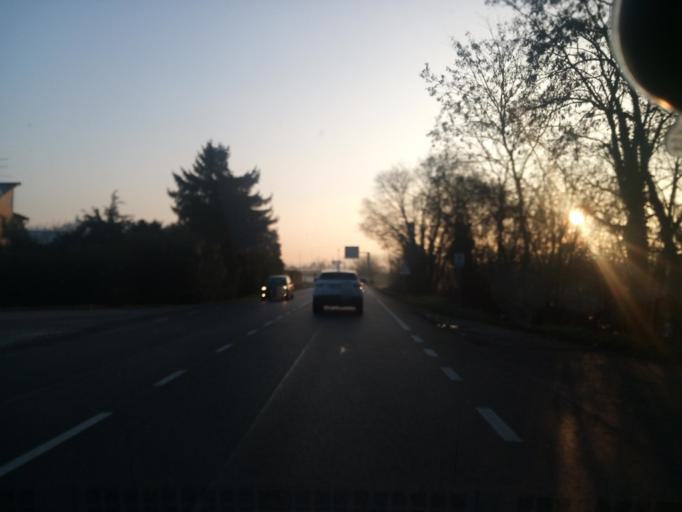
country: IT
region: Veneto
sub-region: Provincia di Vicenza
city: Tezze
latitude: 45.5098
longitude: 11.3842
